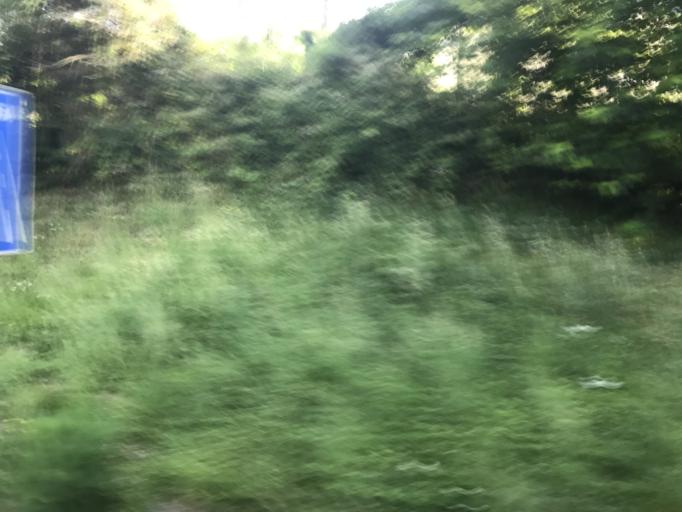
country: ES
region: Basque Country
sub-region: Provincia de Guipuzcoa
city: Tolosa
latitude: 43.1462
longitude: -2.0701
